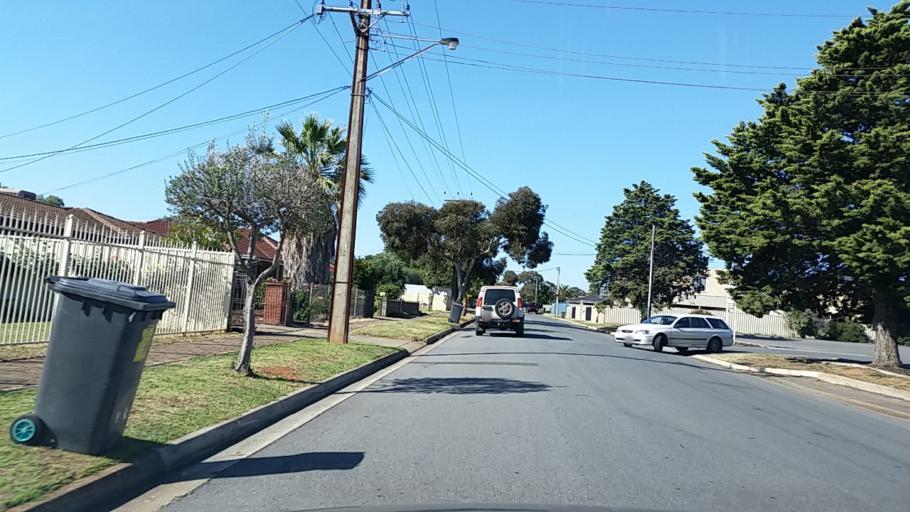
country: AU
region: South Australia
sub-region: Salisbury
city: Salisbury
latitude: -34.7820
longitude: 138.6533
